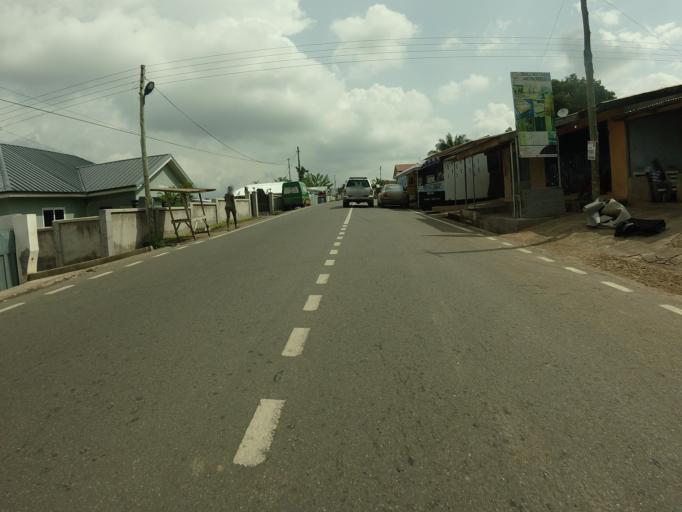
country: GH
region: Volta
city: Ho
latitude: 6.6213
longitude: 0.4789
